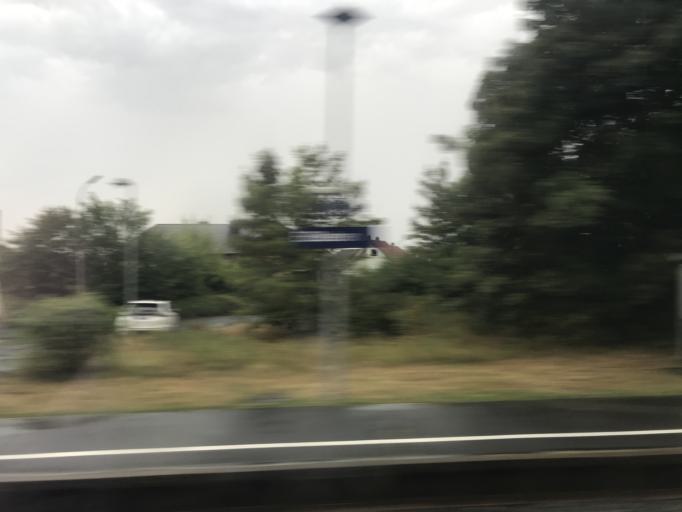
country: DE
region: Bavaria
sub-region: Regierungsbezirk Unterfranken
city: Werneck
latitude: 49.9425
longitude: 10.0852
